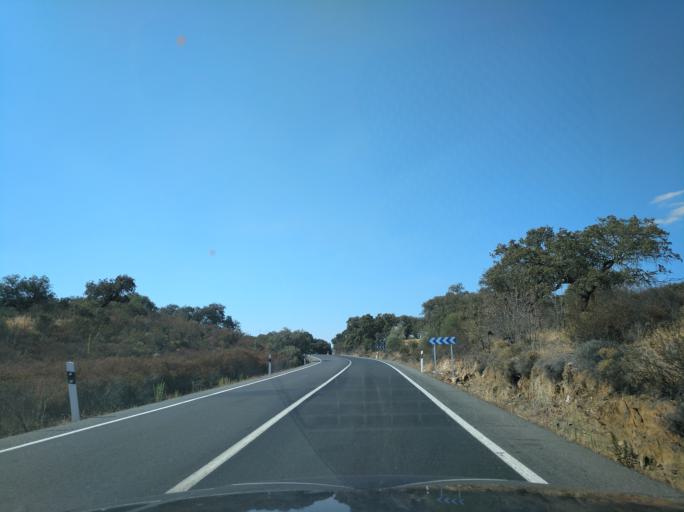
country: ES
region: Andalusia
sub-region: Provincia de Huelva
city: Alosno
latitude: 37.5178
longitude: -7.1330
